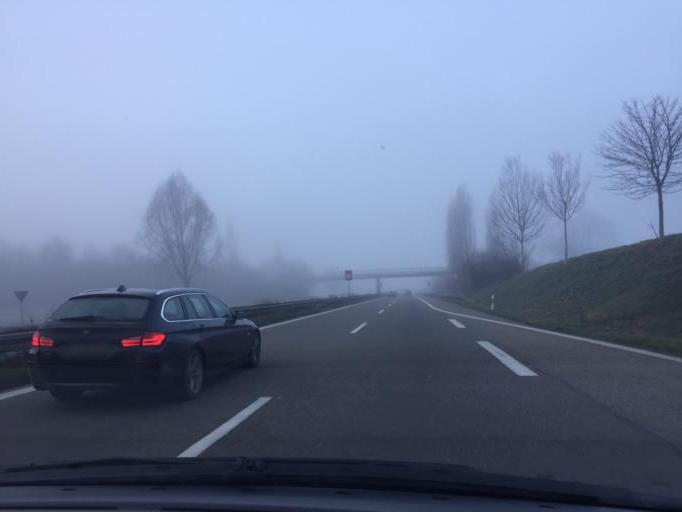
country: DE
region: Baden-Wuerttemberg
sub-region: Freiburg Region
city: Kirchzarten
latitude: 47.9730
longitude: 7.9455
